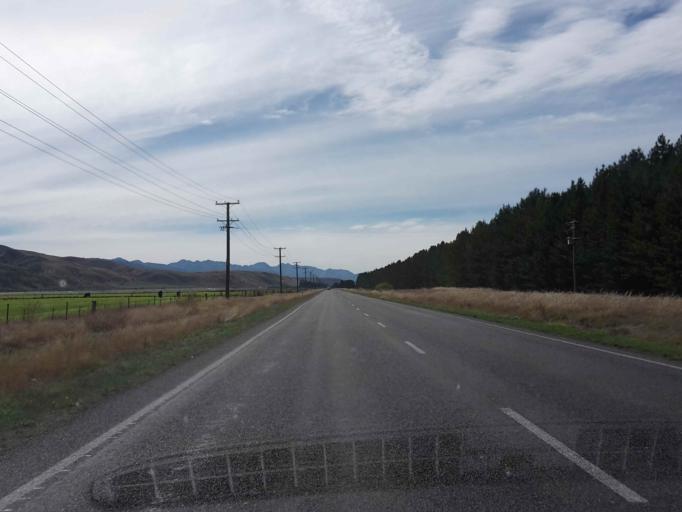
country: NZ
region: Otago
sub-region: Queenstown-Lakes District
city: Wanaka
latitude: -44.4109
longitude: 169.9915
